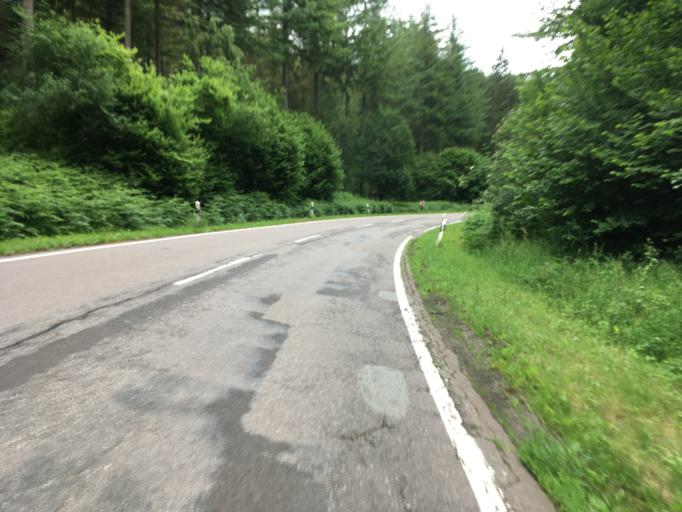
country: DE
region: Saarland
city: Saarhoelzbach
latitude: 49.4961
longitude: 6.6315
